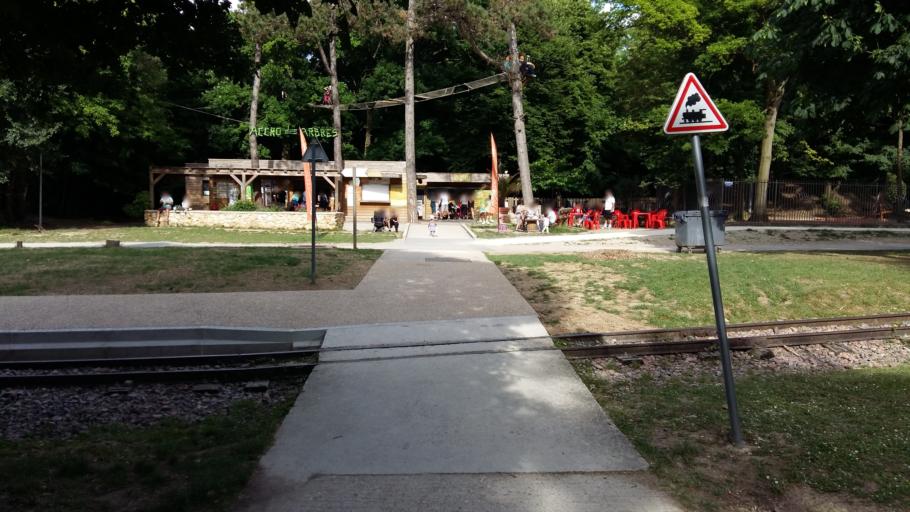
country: FR
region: Ile-de-France
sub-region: Departement de l'Essonne
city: Vigneux-sur-Seine
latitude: 48.6936
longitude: 2.4075
